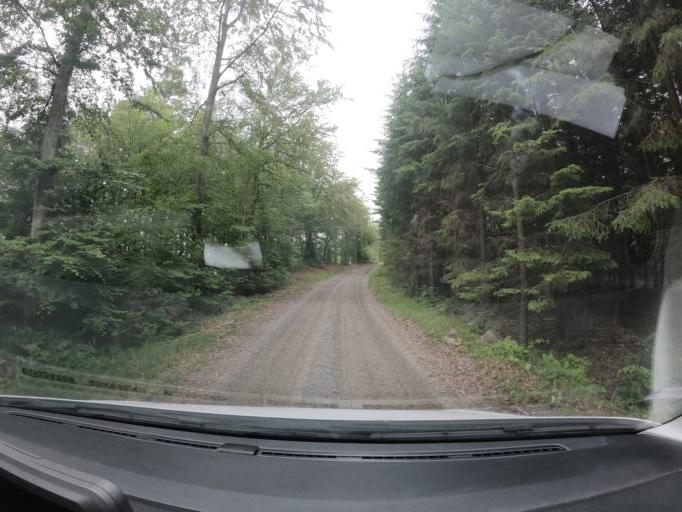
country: SE
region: Skane
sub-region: Perstorps Kommun
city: Perstorp
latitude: 56.1860
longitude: 13.5157
